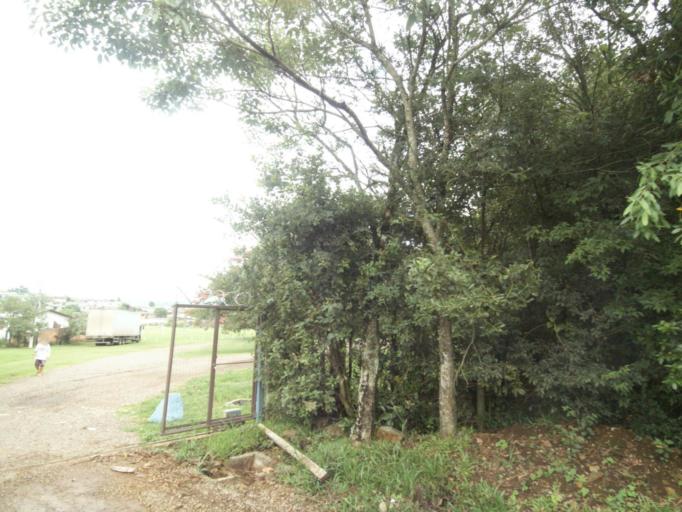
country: BR
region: Rio Grande do Sul
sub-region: Lagoa Vermelha
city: Lagoa Vermelha
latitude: -28.2212
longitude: -51.5234
